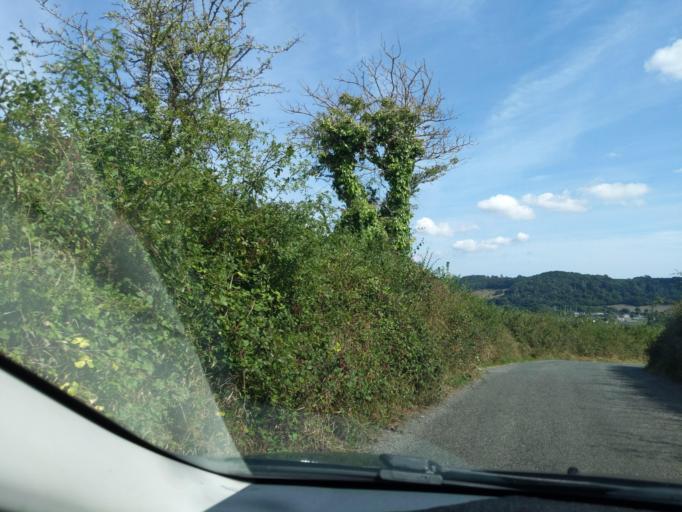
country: GB
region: England
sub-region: Cornwall
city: Torpoint
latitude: 50.3553
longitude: -4.2216
